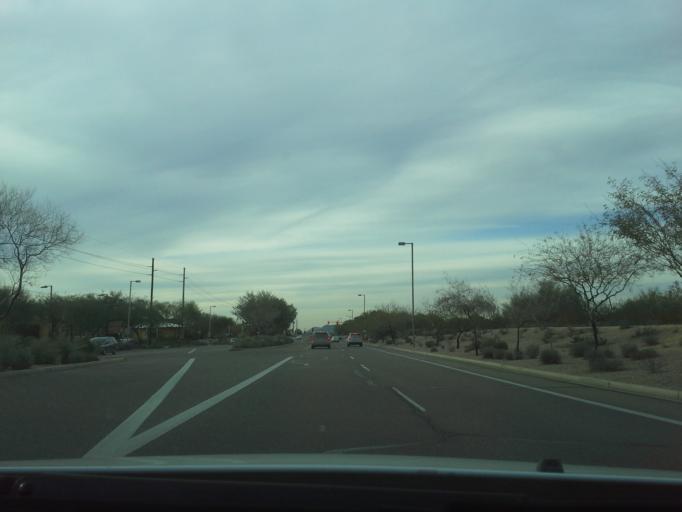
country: US
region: Arizona
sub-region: Maricopa County
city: Paradise Valley
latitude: 33.6798
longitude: -111.9743
